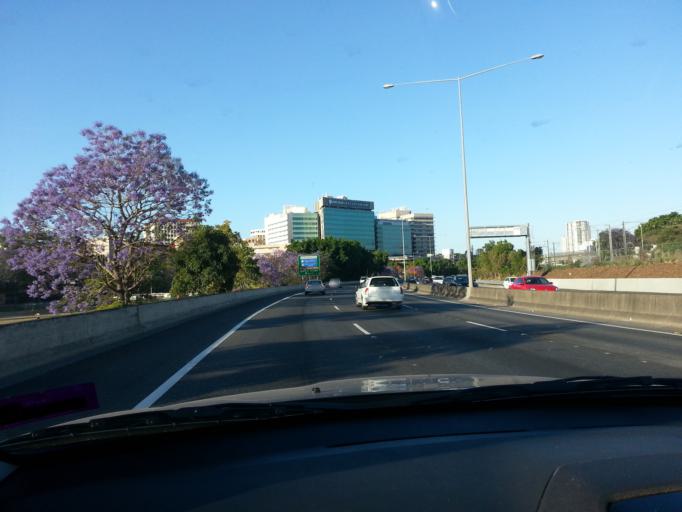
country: AU
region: Queensland
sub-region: Brisbane
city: Spring Hill
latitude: -27.4530
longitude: 153.0242
